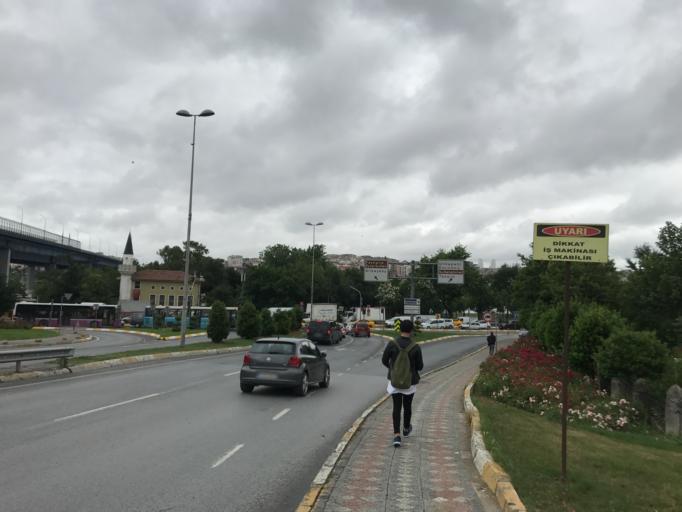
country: TR
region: Istanbul
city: Istanbul
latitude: 41.0398
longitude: 28.9403
